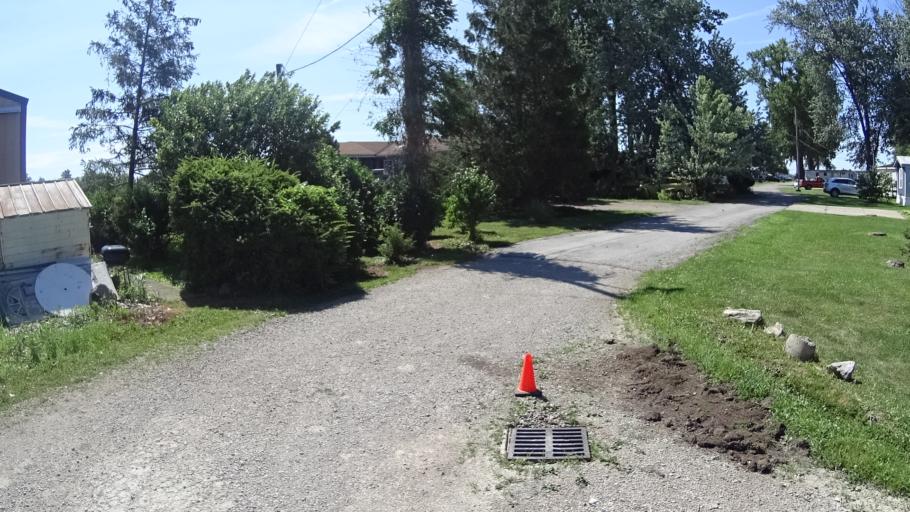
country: US
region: Ohio
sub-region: Ottawa County
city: Port Clinton
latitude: 41.4334
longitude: -82.8934
